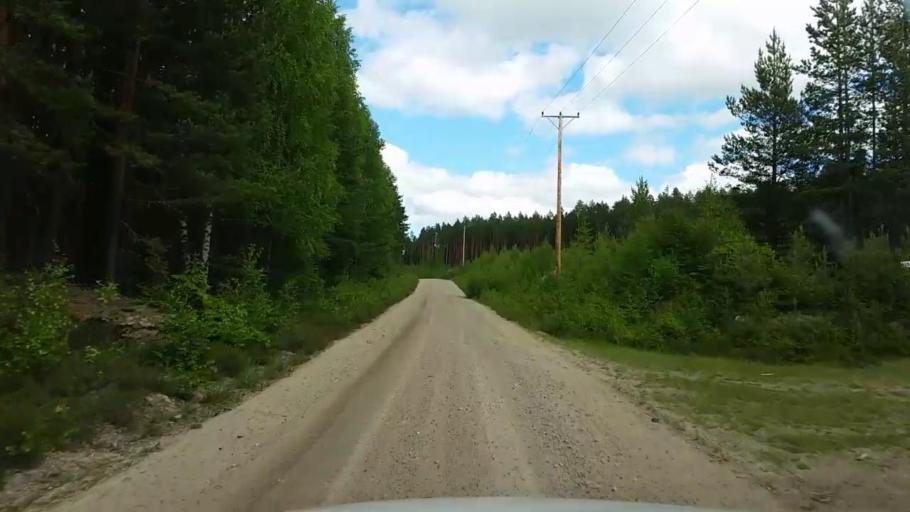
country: SE
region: Gaevleborg
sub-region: Ovanakers Kommun
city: Edsbyn
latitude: 61.5269
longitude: 15.9403
